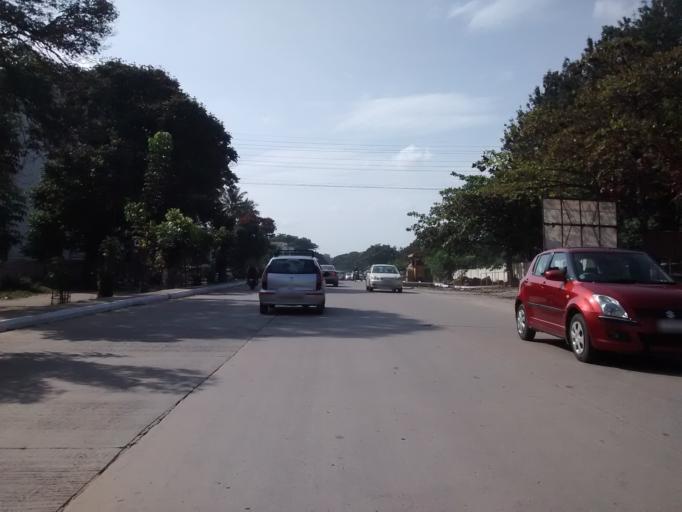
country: IN
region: Karnataka
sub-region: Bangalore Urban
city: Bangalore
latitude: 12.9756
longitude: 77.6559
